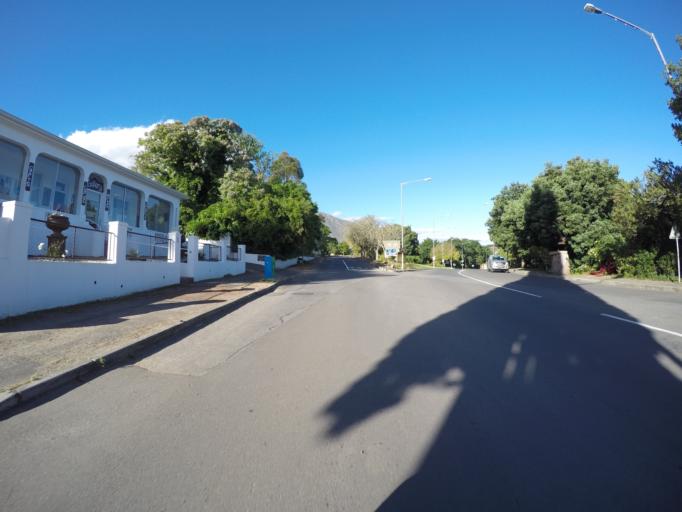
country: ZA
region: Western Cape
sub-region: Overberg District Municipality
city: Swellendam
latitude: -34.0169
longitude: 20.4480
